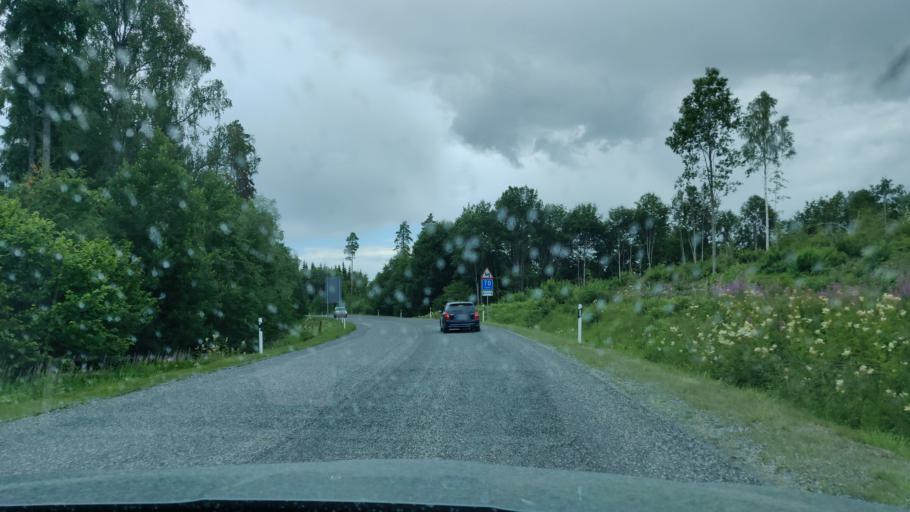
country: EE
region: Vorumaa
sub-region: Antsla vald
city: Vana-Antsla
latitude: 58.0236
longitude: 26.5798
